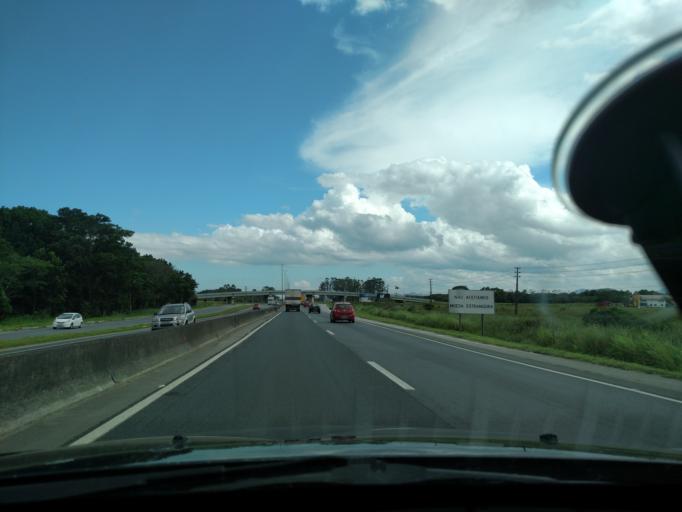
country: BR
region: Santa Catarina
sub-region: Porto Belo
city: Porto Belo
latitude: -27.1593
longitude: -48.6111
